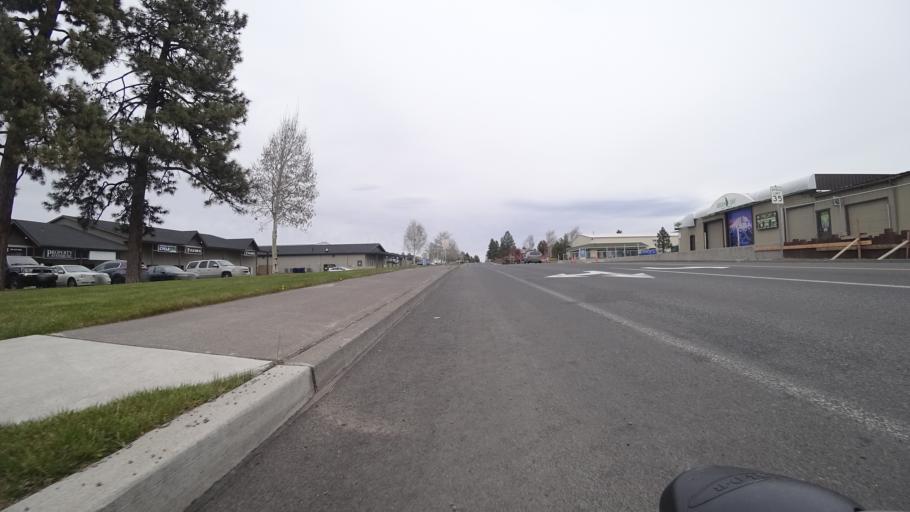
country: US
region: Oregon
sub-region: Deschutes County
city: Bend
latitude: 44.0443
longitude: -121.2926
